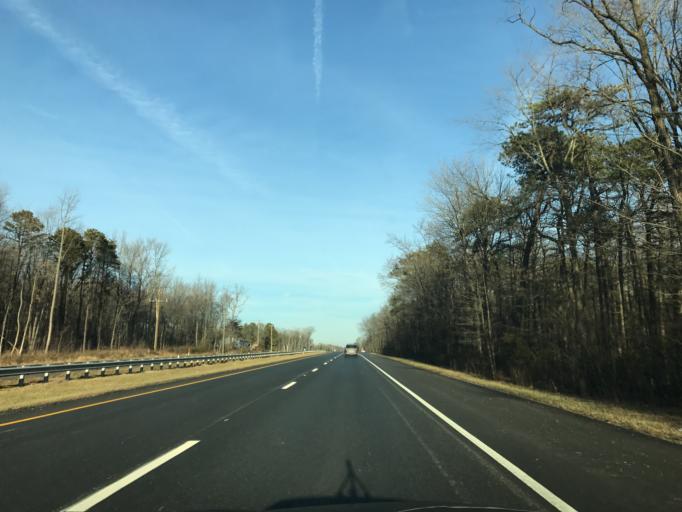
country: US
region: Maryland
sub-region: Cecil County
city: Charlestown
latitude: 39.5922
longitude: -75.9913
